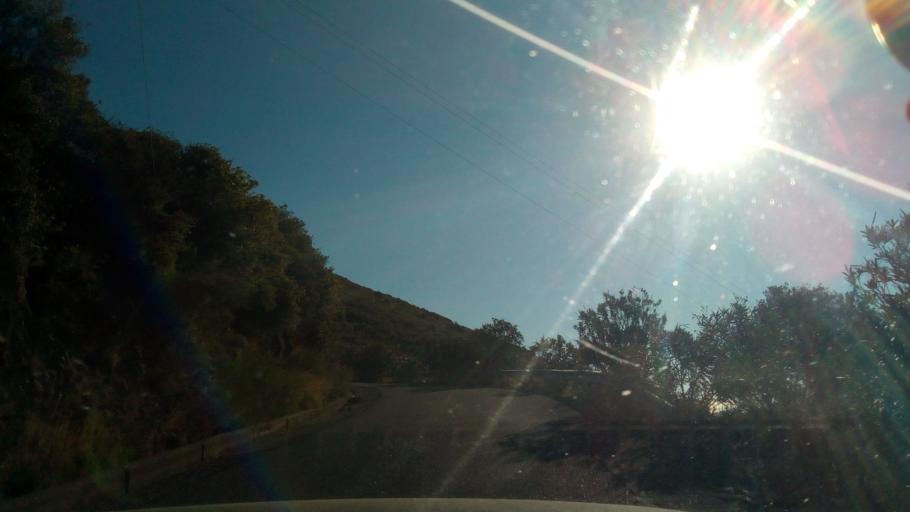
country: GR
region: West Greece
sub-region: Nomos Aitolias kai Akarnanias
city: Nafpaktos
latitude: 38.4151
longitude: 21.8437
